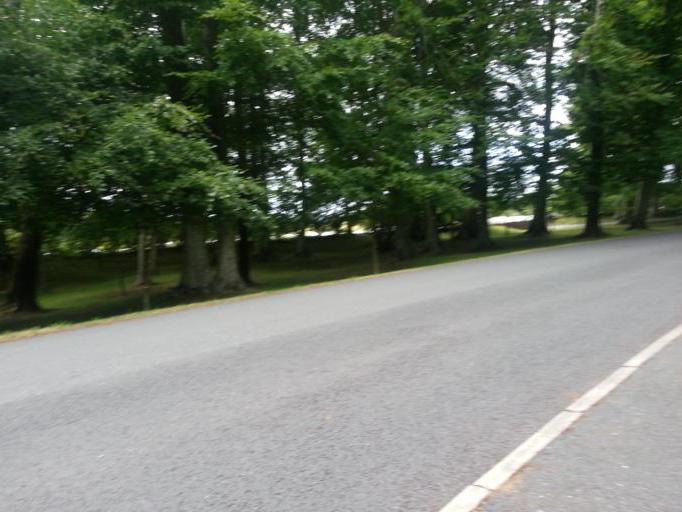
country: IE
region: Leinster
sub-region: Wicklow
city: Enniskerry
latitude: 53.1863
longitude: -6.1855
